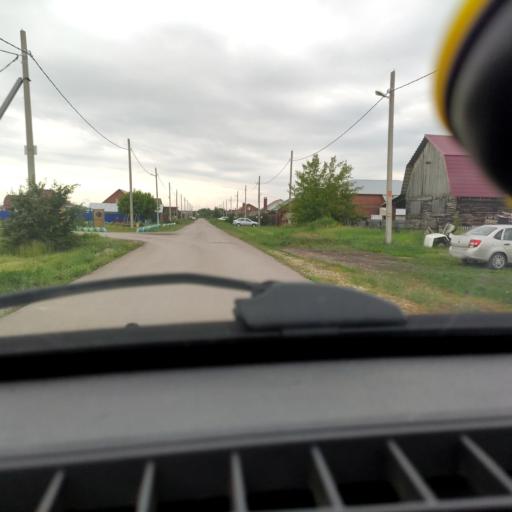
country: RU
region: Samara
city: Zhigulevsk
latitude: 53.5524
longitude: 49.5186
